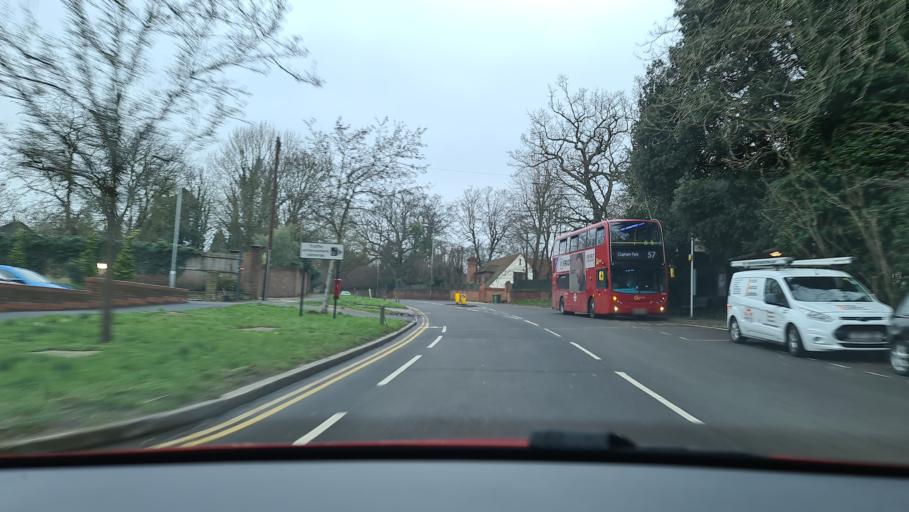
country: GB
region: England
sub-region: Greater London
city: New Malden
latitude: 51.4163
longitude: -0.2541
